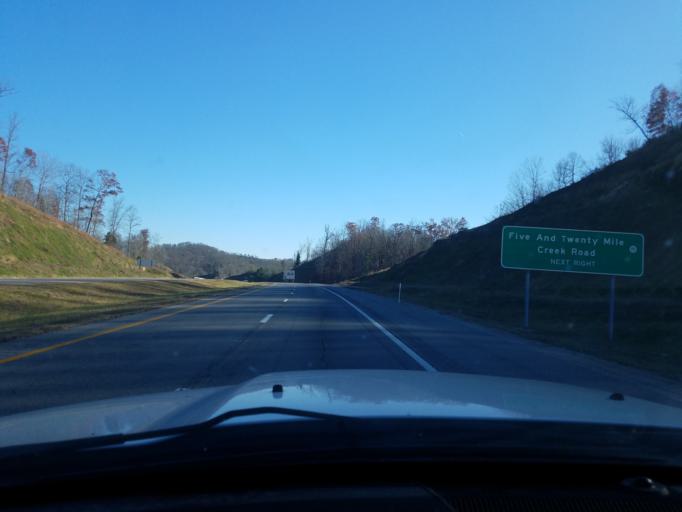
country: US
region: West Virginia
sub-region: Putnam County
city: Buffalo
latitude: 38.5603
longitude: -82.0098
